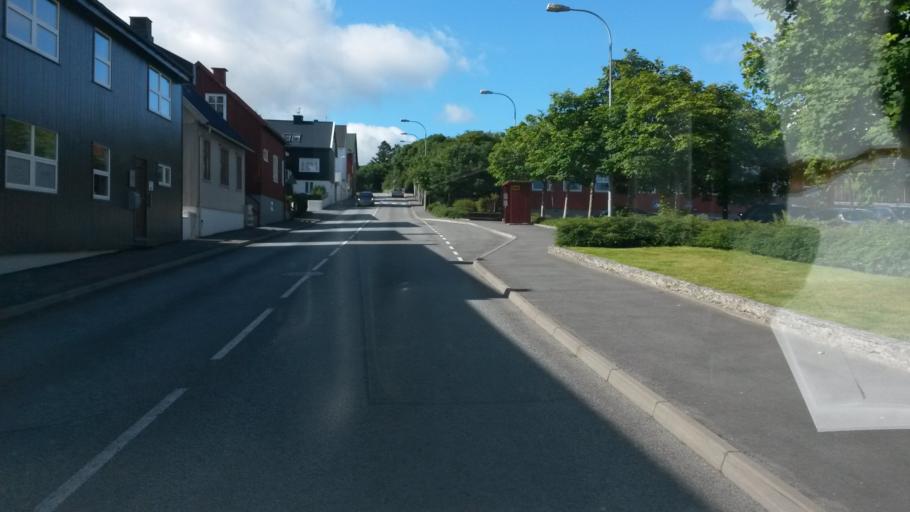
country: FO
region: Streymoy
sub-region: Torshavn
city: Torshavn
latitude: 62.0102
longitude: -6.7666
